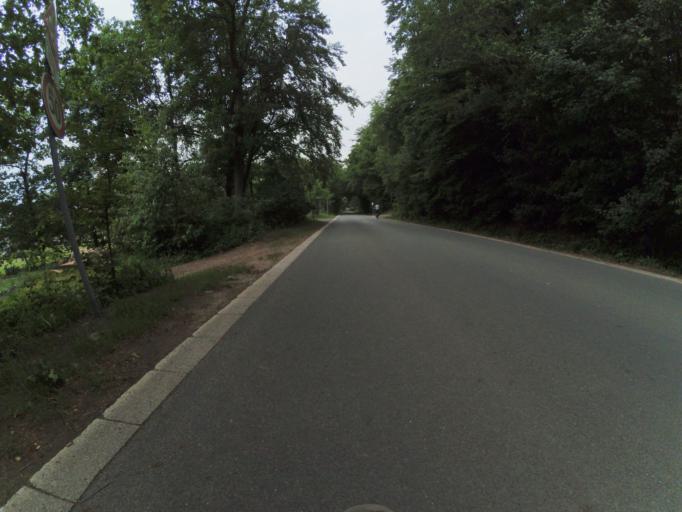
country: DE
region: North Rhine-Westphalia
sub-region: Regierungsbezirk Munster
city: Horstel
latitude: 52.3198
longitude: 7.6362
